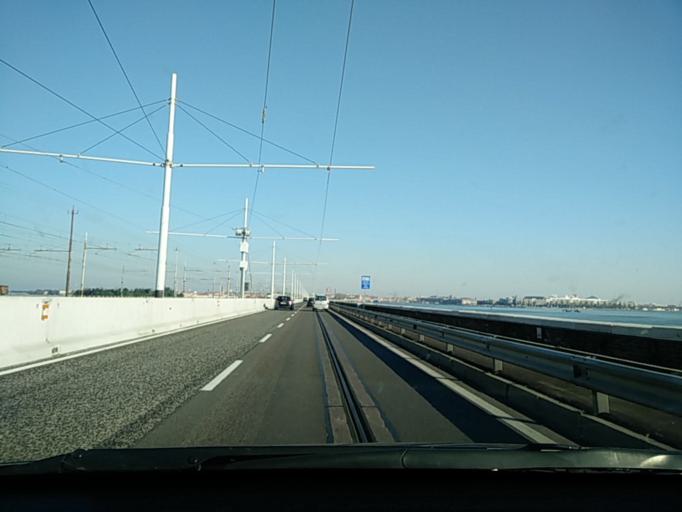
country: IT
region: Veneto
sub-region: Provincia di Venezia
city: Campalto
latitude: 45.4536
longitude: 12.2988
